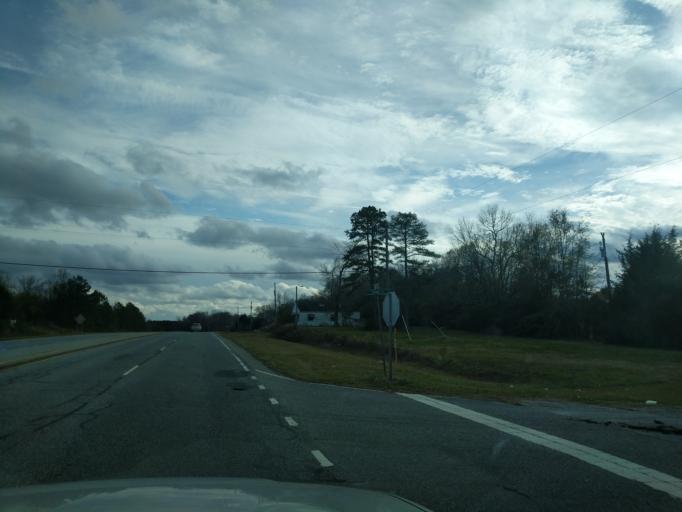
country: US
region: South Carolina
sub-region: Greenwood County
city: Ware Shoals
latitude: 34.4946
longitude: -82.2865
